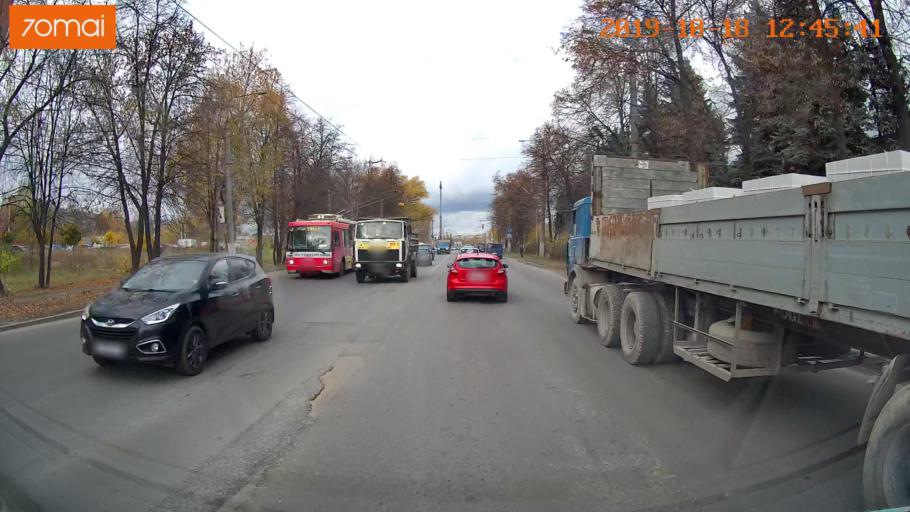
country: RU
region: Rjazan
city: Ryazan'
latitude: 54.6536
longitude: 39.6656
